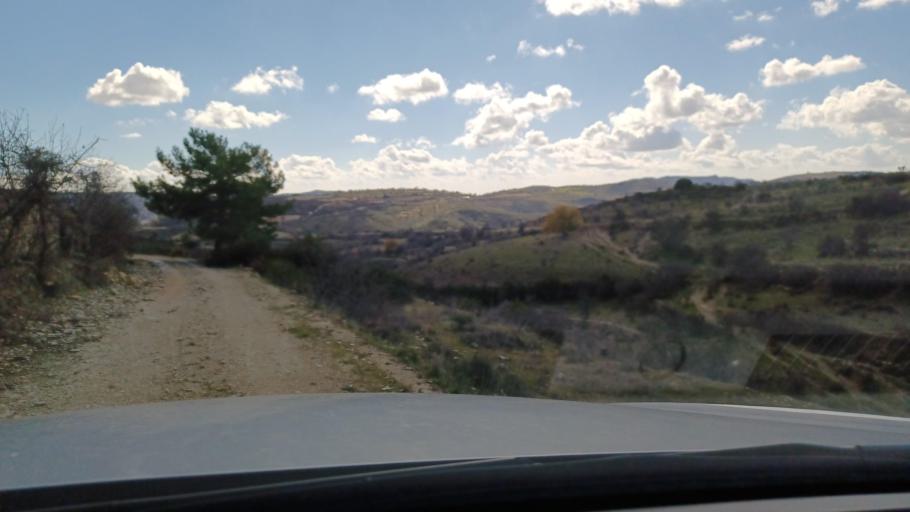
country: CY
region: Limassol
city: Pachna
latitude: 34.8201
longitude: 32.7672
